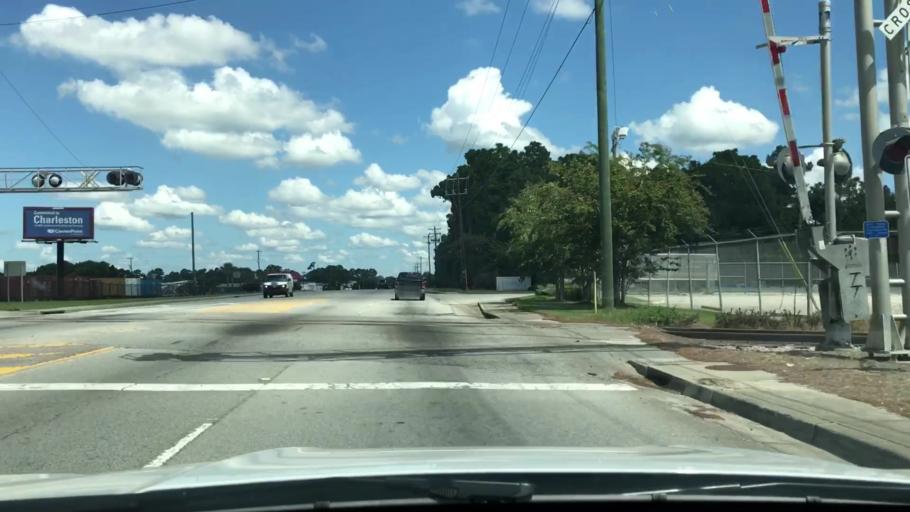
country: US
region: South Carolina
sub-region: Berkeley County
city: Hanahan
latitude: 32.9070
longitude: -79.9857
